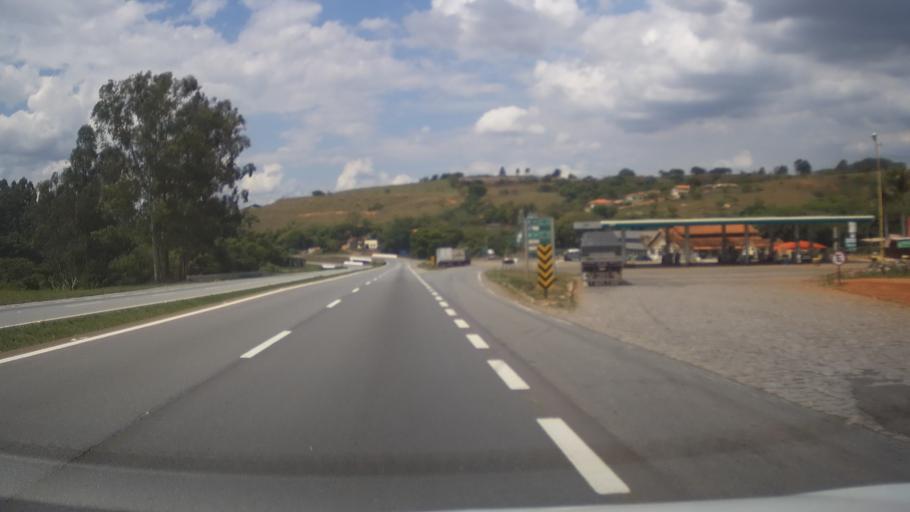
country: BR
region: Minas Gerais
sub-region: Nepomuceno
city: Nepomuceno
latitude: -21.3014
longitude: -45.1531
